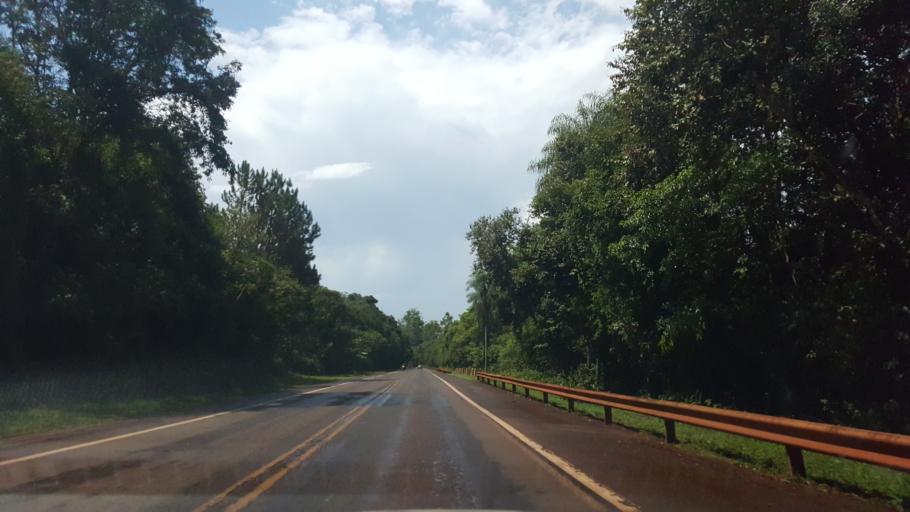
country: AR
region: Misiones
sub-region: Departamento de Eldorado
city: Eldorado
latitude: -26.3576
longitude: -54.6186
